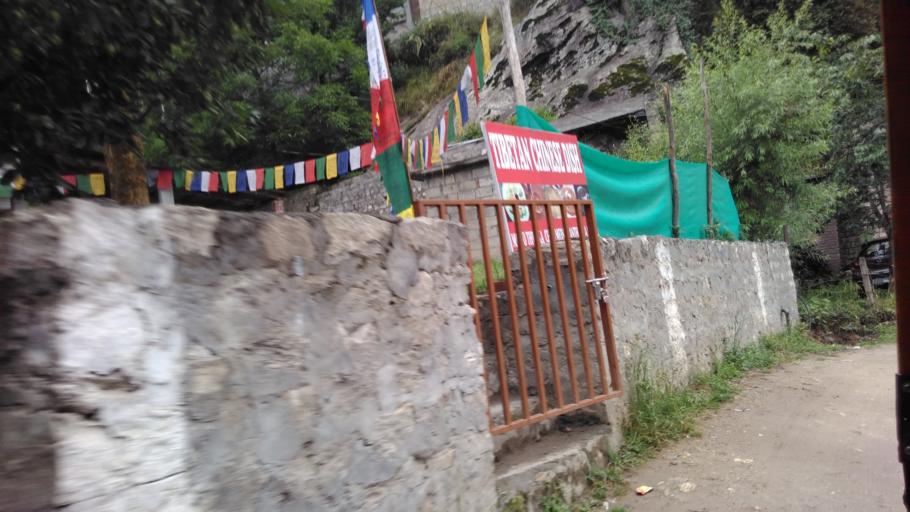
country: IN
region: Himachal Pradesh
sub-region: Kulu
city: Manali
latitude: 32.2220
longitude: 77.1848
